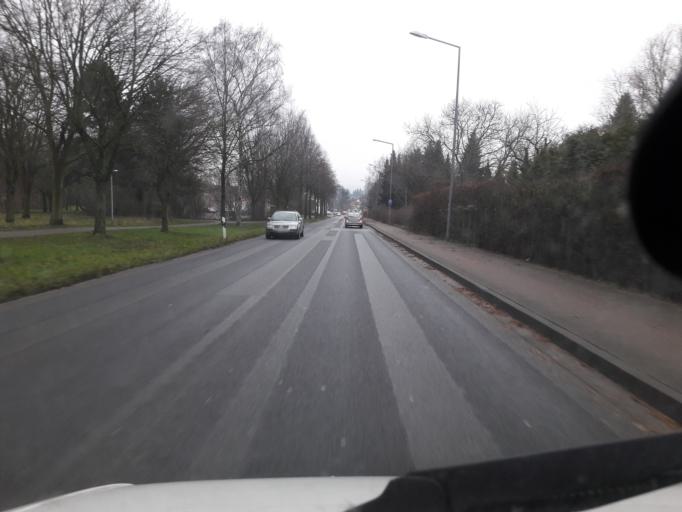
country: DE
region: North Rhine-Westphalia
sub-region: Regierungsbezirk Detmold
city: Minden
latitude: 52.2764
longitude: 8.8882
